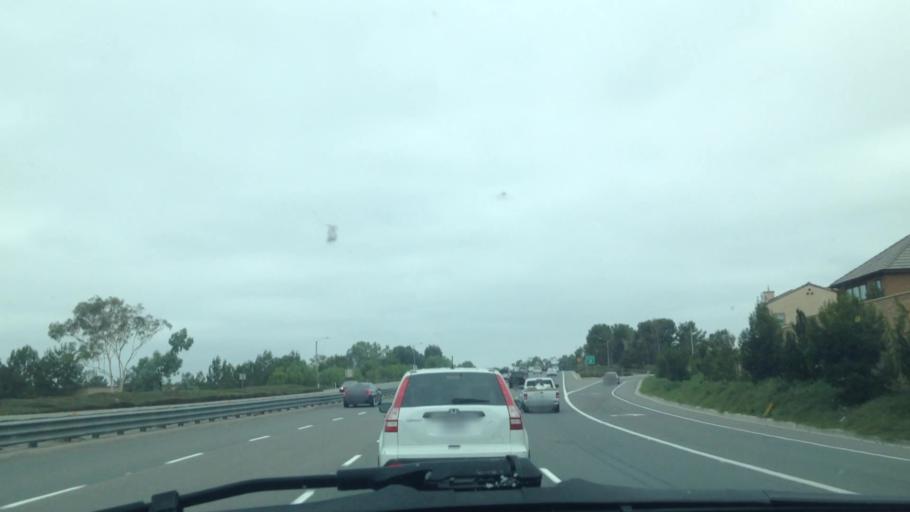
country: US
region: California
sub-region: Orange County
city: Irvine
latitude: 33.6985
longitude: -117.8149
